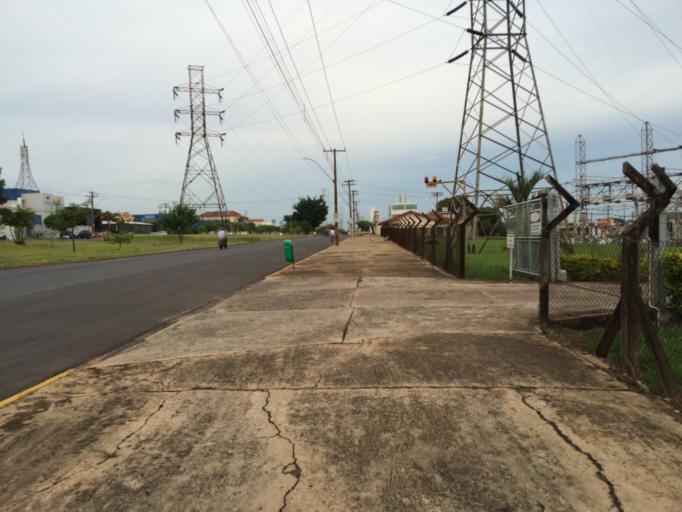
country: BR
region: Sao Paulo
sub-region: Matao
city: Matao
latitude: -21.6162
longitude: -48.3642
